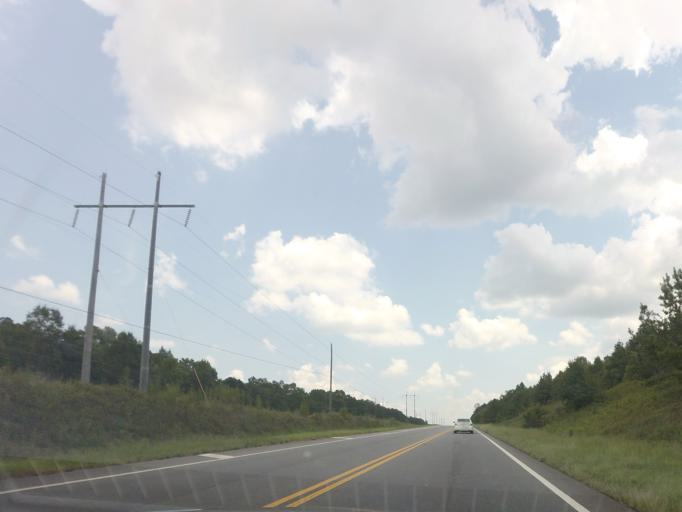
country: US
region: Georgia
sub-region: Houston County
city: Robins Air Force Base
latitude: 32.5416
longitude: -83.5045
